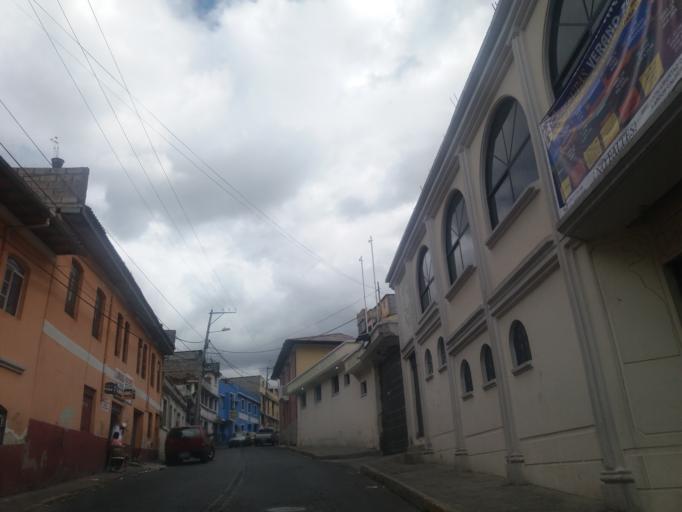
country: EC
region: Pichincha
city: Quito
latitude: -0.2206
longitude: -78.5243
